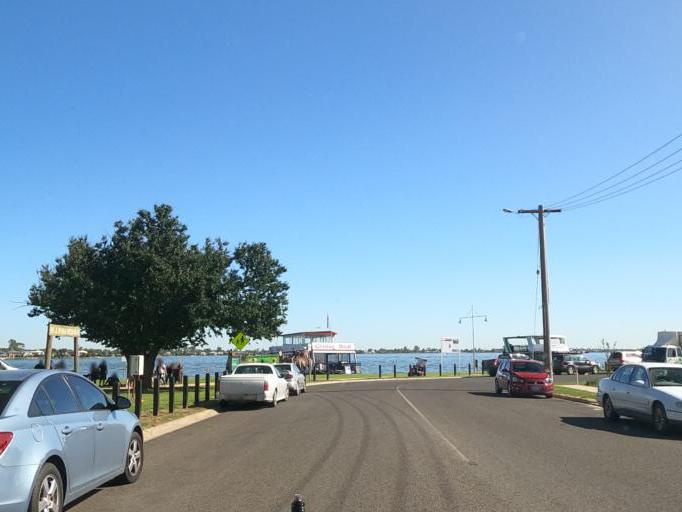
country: AU
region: Victoria
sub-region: Moira
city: Yarrawonga
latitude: -36.0077
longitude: 146.0086
